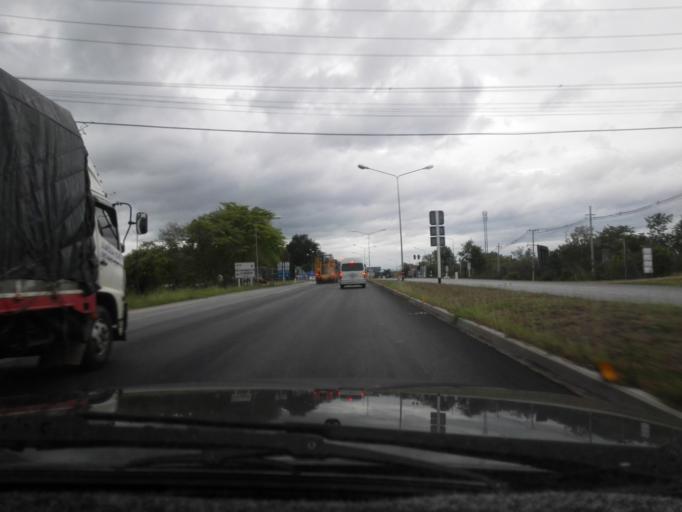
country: TH
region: Tak
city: Tak
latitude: 16.8400
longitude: 99.1145
